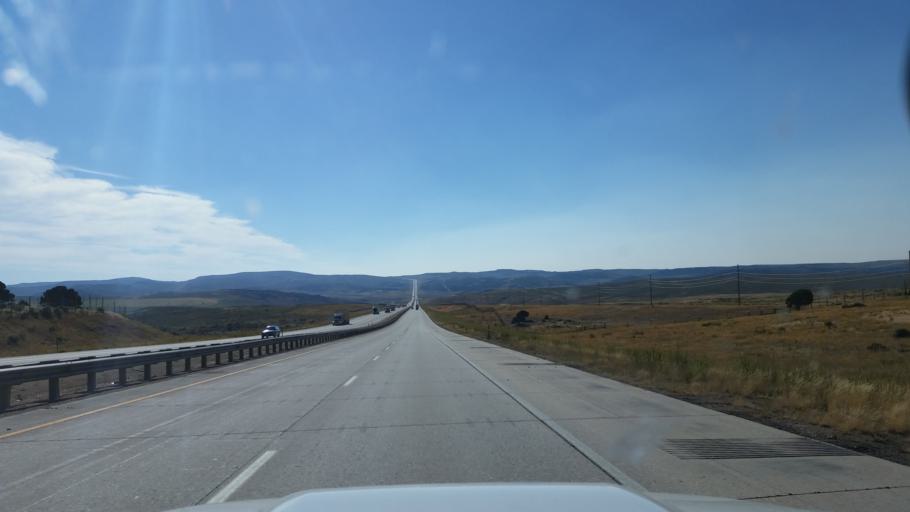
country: US
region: Wyoming
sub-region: Uinta County
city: Mountain View
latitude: 41.2978
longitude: -110.5828
